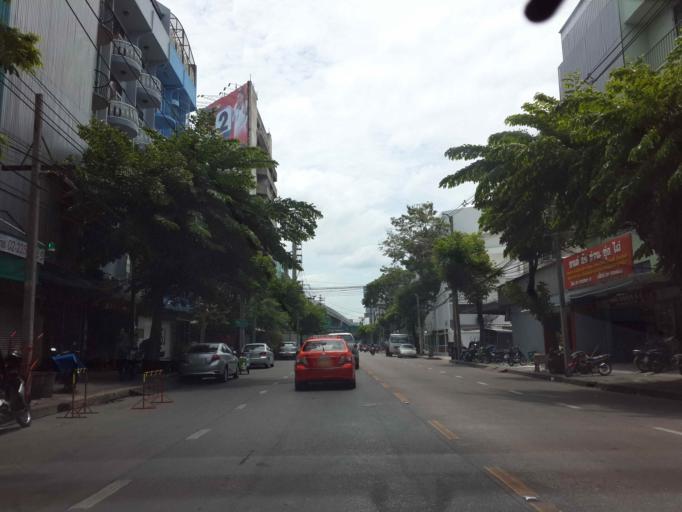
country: TH
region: Bangkok
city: Samphanthawong
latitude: 13.7345
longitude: 100.5187
